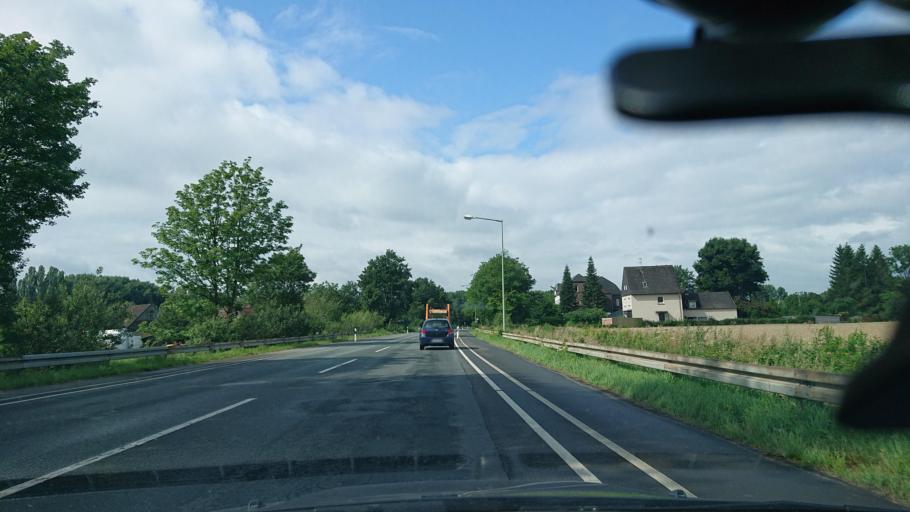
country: DE
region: North Rhine-Westphalia
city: Lunen
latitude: 51.6173
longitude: 7.5630
